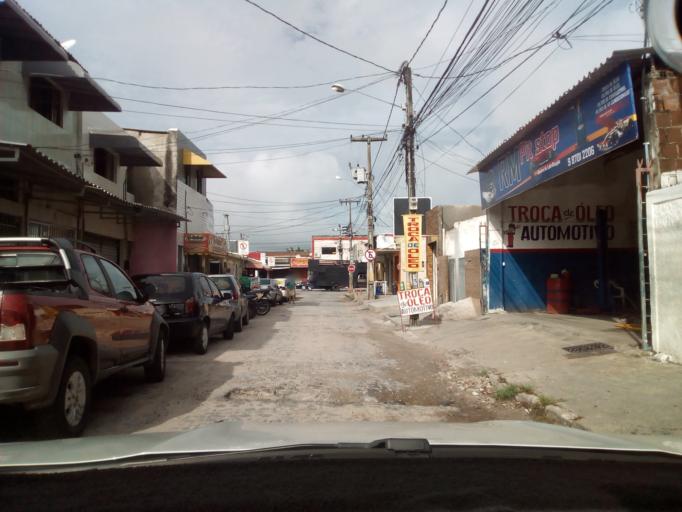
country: BR
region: Paraiba
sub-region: Joao Pessoa
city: Joao Pessoa
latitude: -7.1675
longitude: -34.8391
